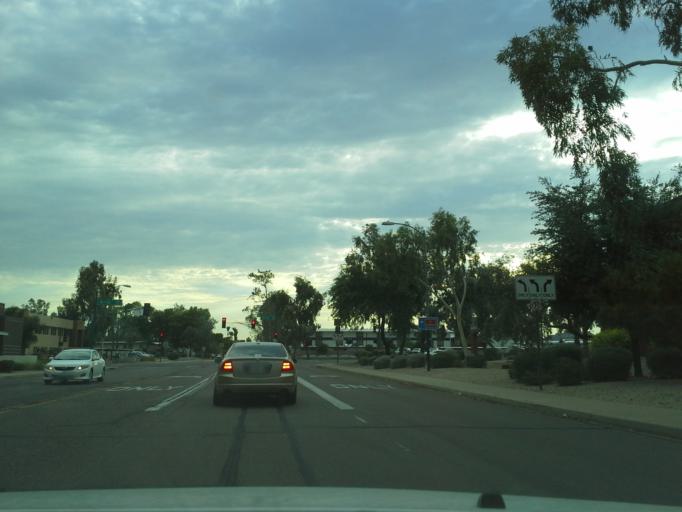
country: US
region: Arizona
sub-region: Maricopa County
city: Phoenix
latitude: 33.5129
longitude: -112.0465
